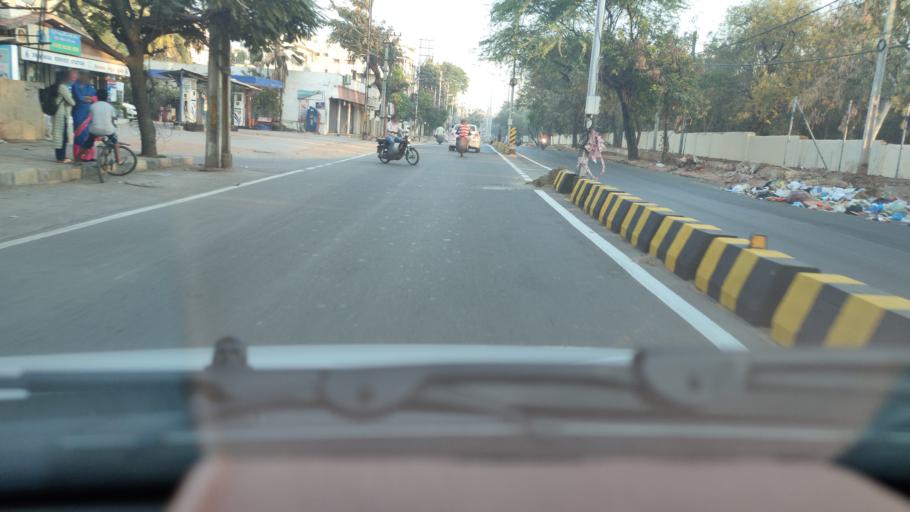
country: IN
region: Telangana
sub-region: Rangareddi
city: Gaddi Annaram
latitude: 17.3871
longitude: 78.5165
